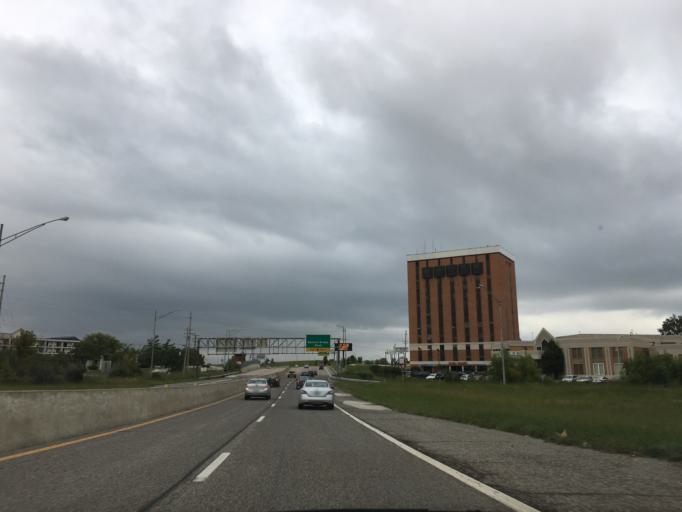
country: US
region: Missouri
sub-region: Saint Louis County
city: Saint Ann
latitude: 38.7446
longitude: -90.3949
